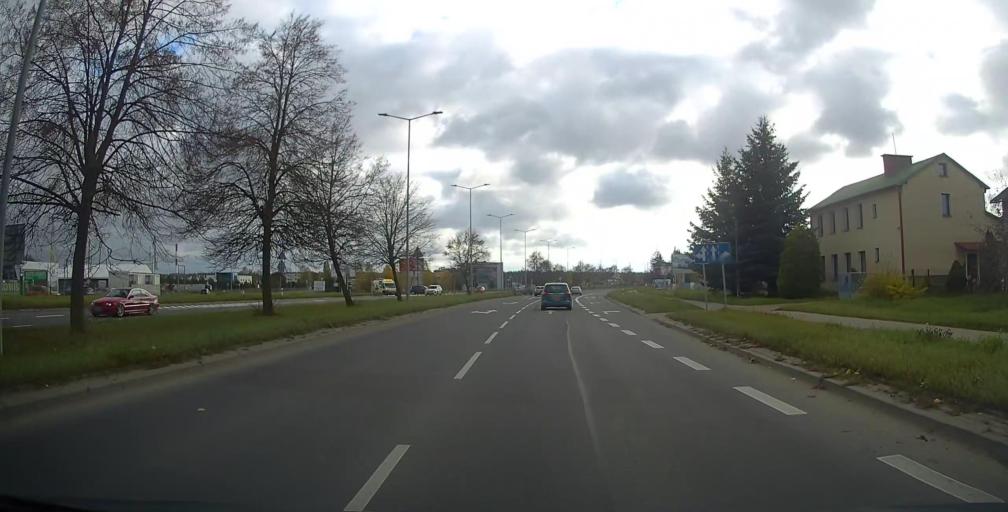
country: PL
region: Warmian-Masurian Voivodeship
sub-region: Powiat elcki
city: Elk
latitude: 53.8317
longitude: 22.3915
